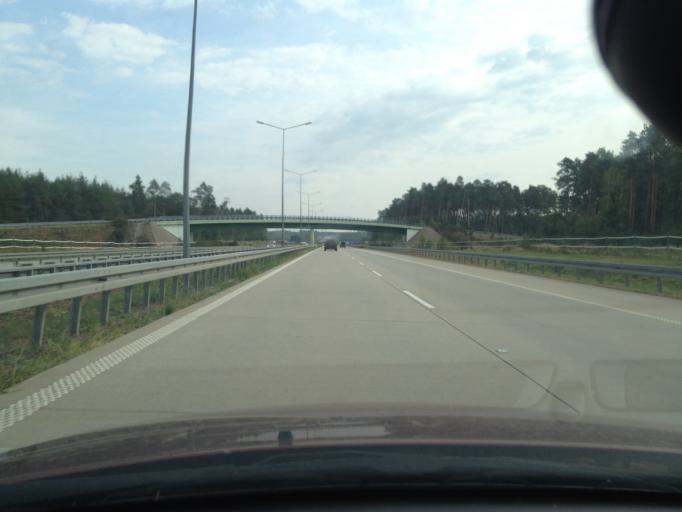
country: PL
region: Lower Silesian Voivodeship
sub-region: Powiat boleslawiecki
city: Nowogrodziec
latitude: 51.2426
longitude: 15.3384
